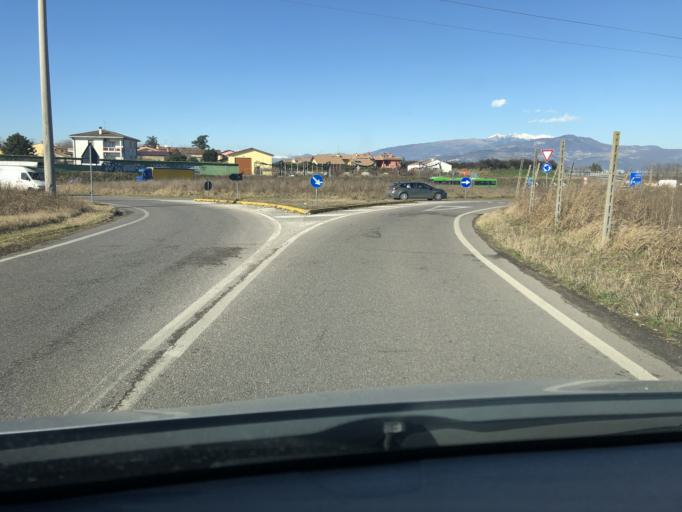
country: IT
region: Veneto
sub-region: Provincia di Verona
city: Bassone
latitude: 45.4538
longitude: 10.8783
